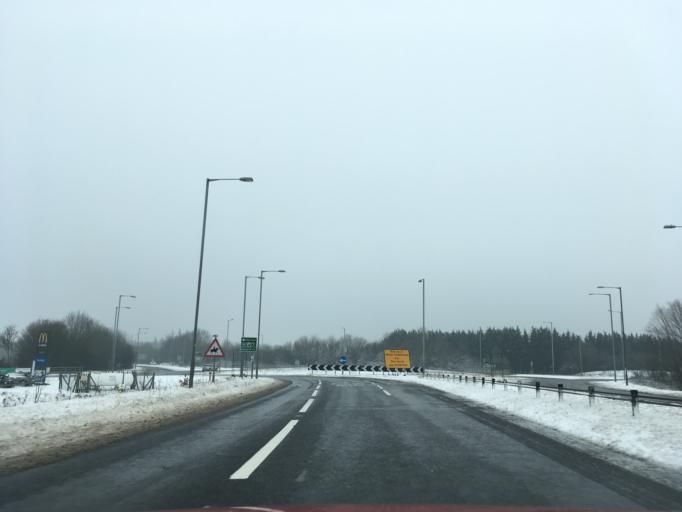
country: GB
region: England
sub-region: Warwickshire
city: Alcester
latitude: 52.2045
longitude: -1.8755
